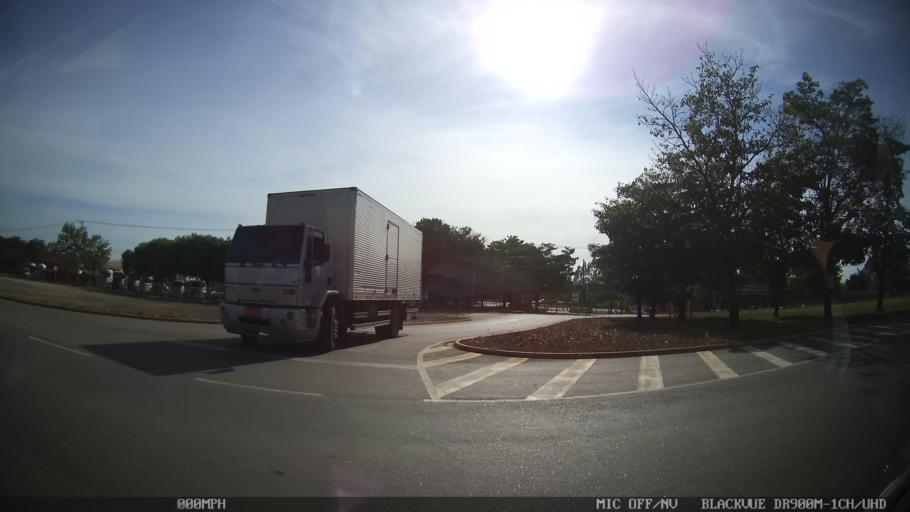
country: BR
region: Sao Paulo
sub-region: Rio Das Pedras
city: Rio das Pedras
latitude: -22.7934
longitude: -47.6204
